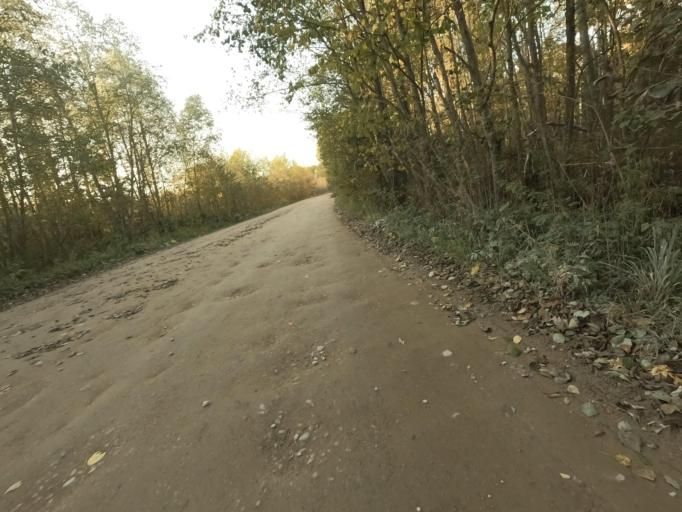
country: RU
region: Leningrad
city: Lyuban'
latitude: 59.0014
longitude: 31.0994
